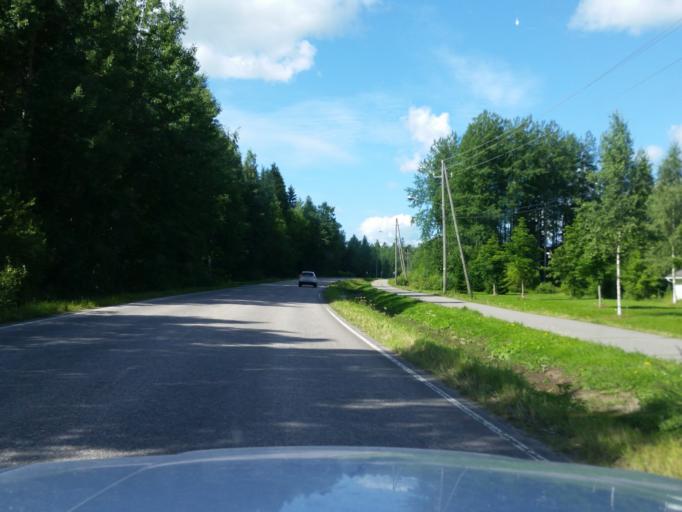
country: FI
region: Uusimaa
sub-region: Helsinki
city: Vihti
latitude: 60.3282
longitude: 24.3142
